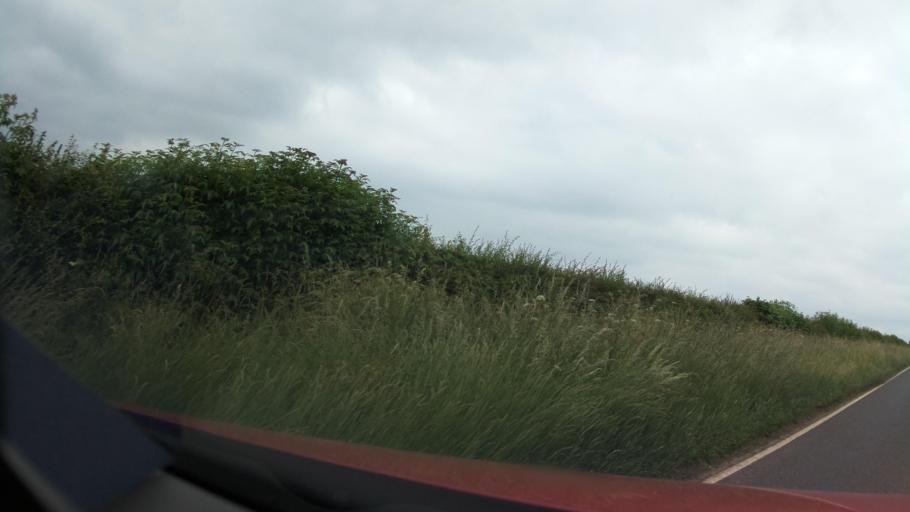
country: GB
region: England
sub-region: District of Rutland
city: Empingham
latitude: 52.6663
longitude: -0.6213
